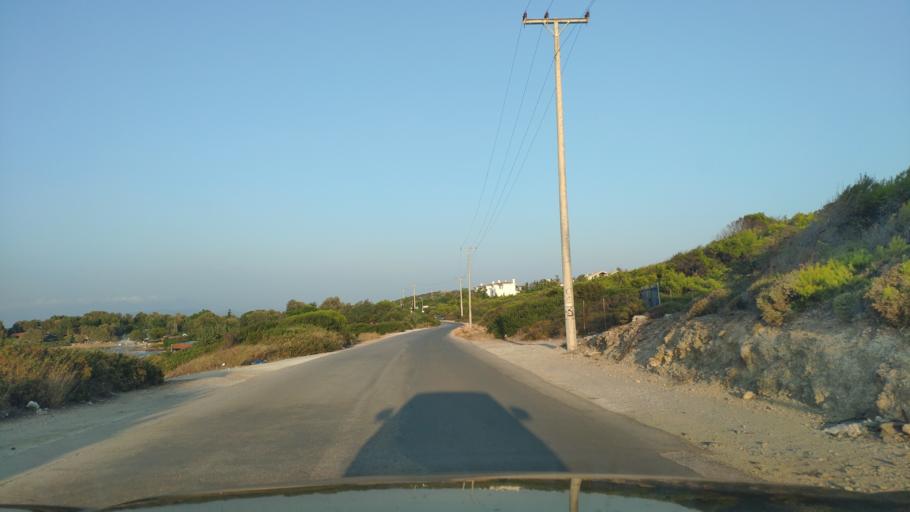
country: GR
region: Attica
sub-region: Nomarchia Anatolikis Attikis
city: Limin Mesoyaias
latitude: 37.9217
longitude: 24.0168
